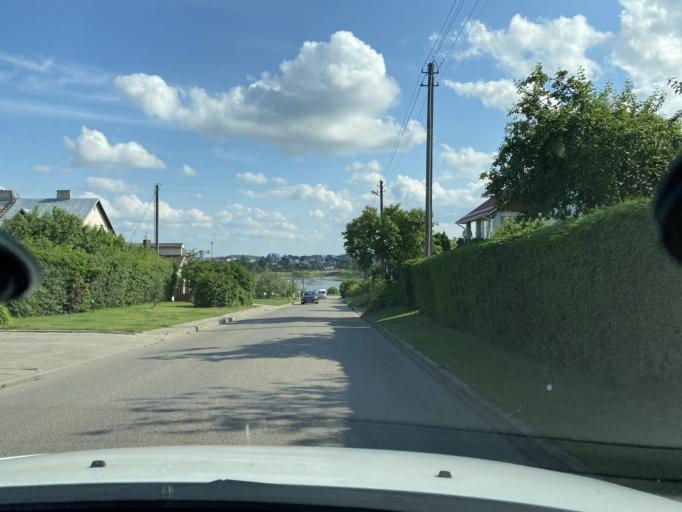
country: LT
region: Vilnius County
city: Pasilaiciai
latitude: 54.7375
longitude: 25.1982
